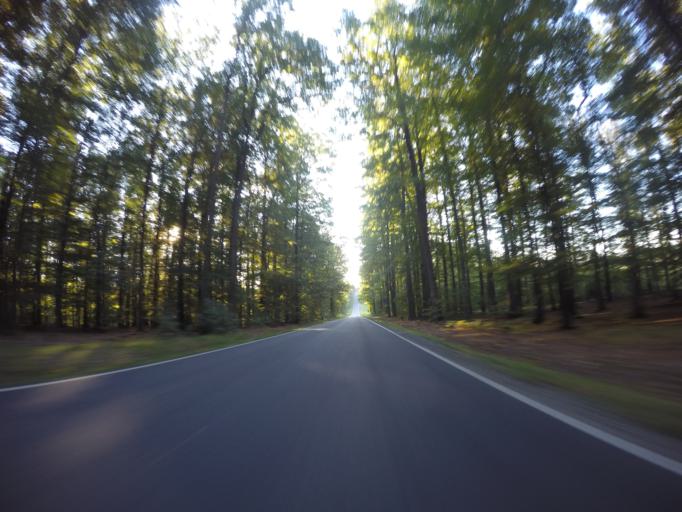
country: DE
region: Bavaria
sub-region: Regierungsbezirk Unterfranken
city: Altenbuch
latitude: 49.8702
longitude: 9.4092
